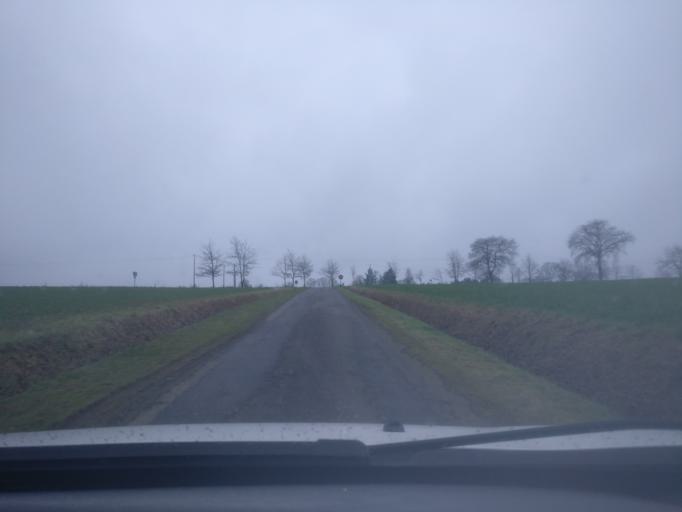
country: FR
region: Brittany
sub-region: Departement d'Ille-et-Vilaine
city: Chasne-sur-Illet
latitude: 48.2911
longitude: -1.5834
